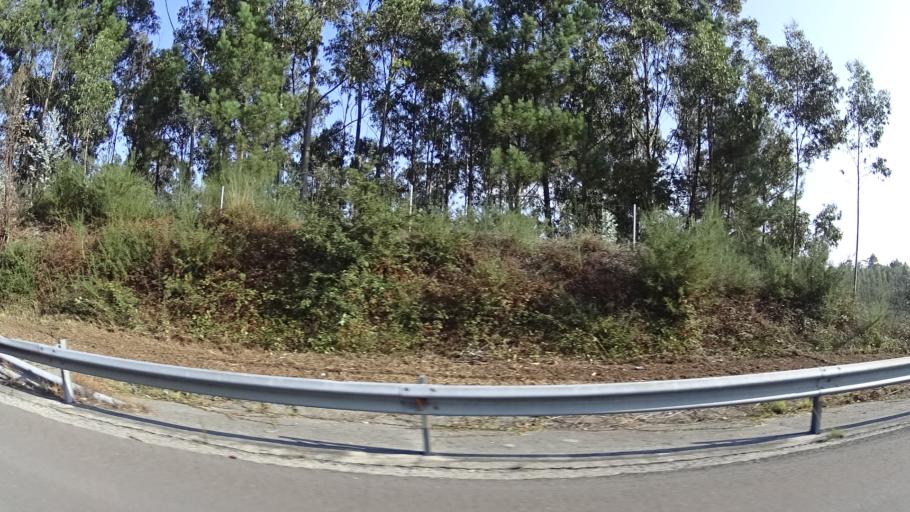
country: ES
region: Galicia
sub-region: Provincia da Coruna
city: Coiros
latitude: 43.2454
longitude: -8.1482
